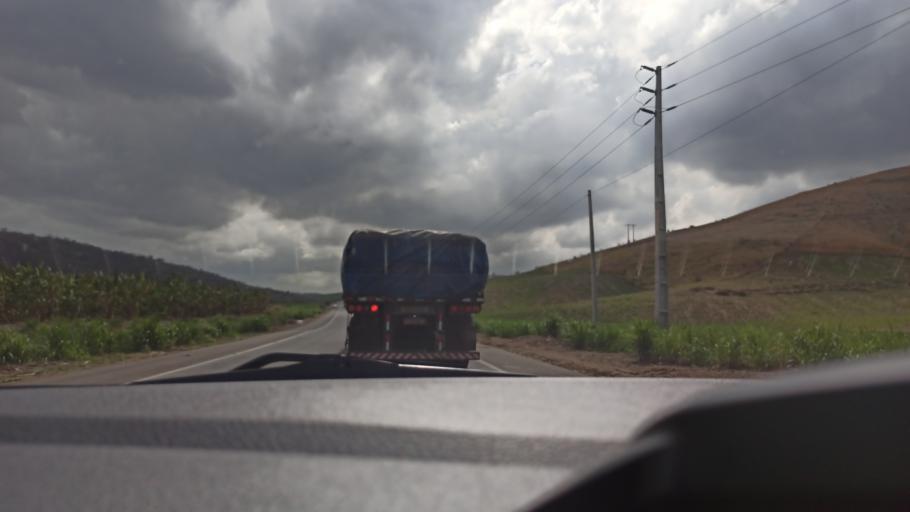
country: BR
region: Pernambuco
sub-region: Timbauba
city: Timbauba
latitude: -7.5225
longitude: -35.2993
